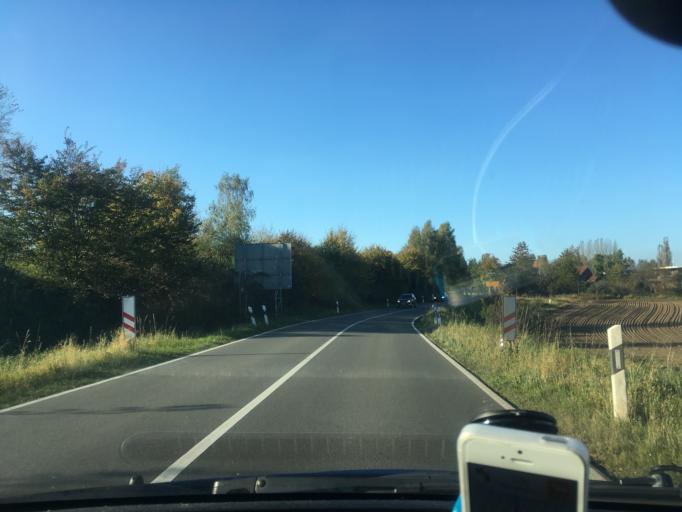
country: DE
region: Mecklenburg-Vorpommern
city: Zarrentin
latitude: 53.5422
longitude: 10.9306
